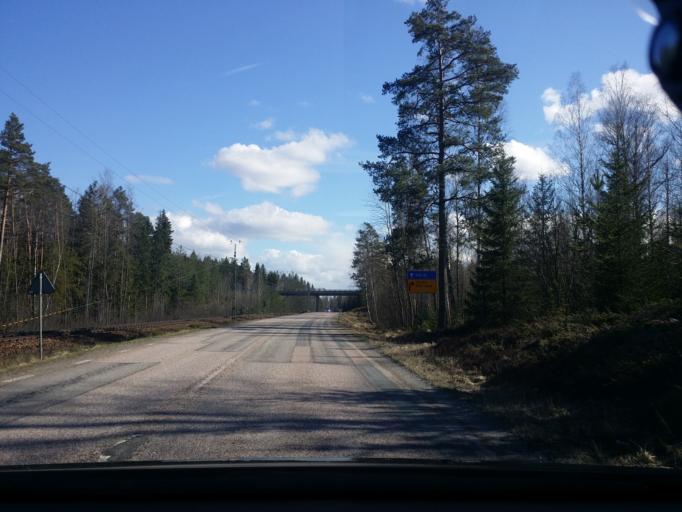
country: SE
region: Vaestmanland
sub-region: Sala Kommun
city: Sala
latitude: 59.9707
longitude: 16.5028
